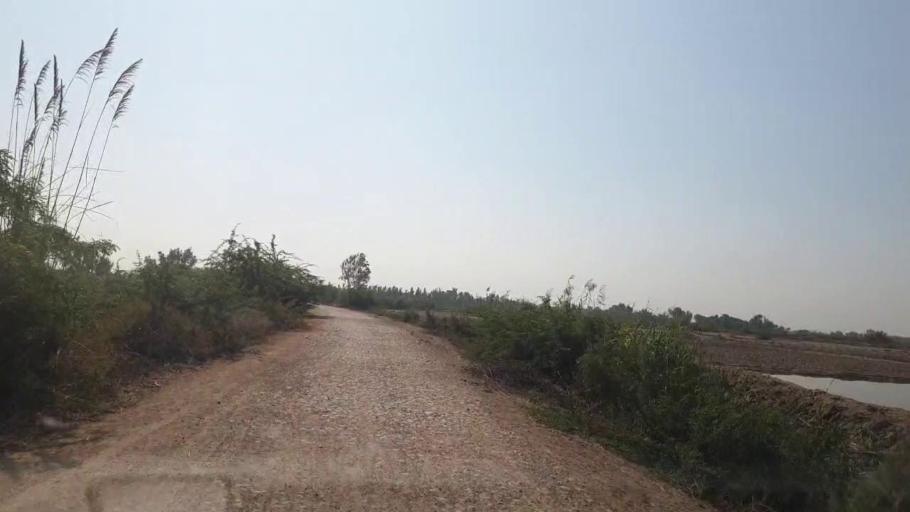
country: PK
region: Sindh
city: Gharo
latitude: 24.6821
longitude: 67.7494
